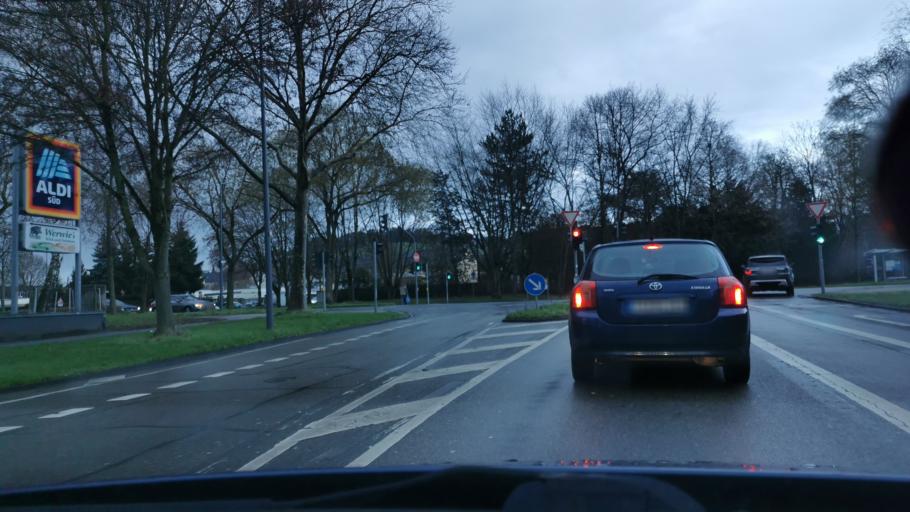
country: DE
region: Rheinland-Pfalz
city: Trier
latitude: 49.7416
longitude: 6.6447
